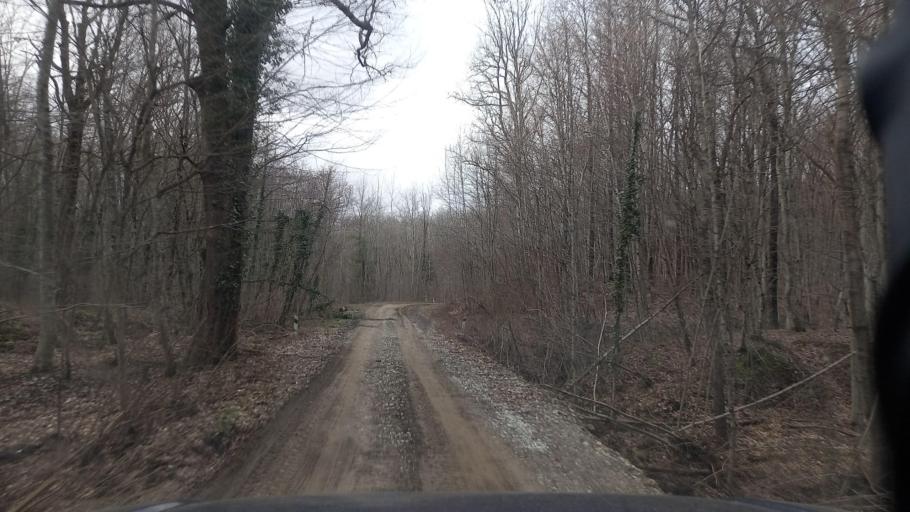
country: RU
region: Krasnodarskiy
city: Dzhubga
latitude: 44.4857
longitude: 38.7836
